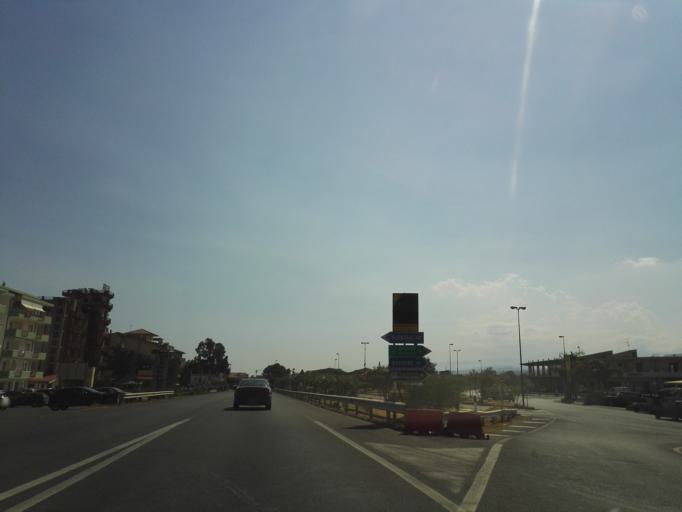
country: IT
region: Calabria
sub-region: Provincia di Reggio Calabria
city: Marina di Gioiosa Ionica
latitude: 38.2938
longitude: 16.3211
